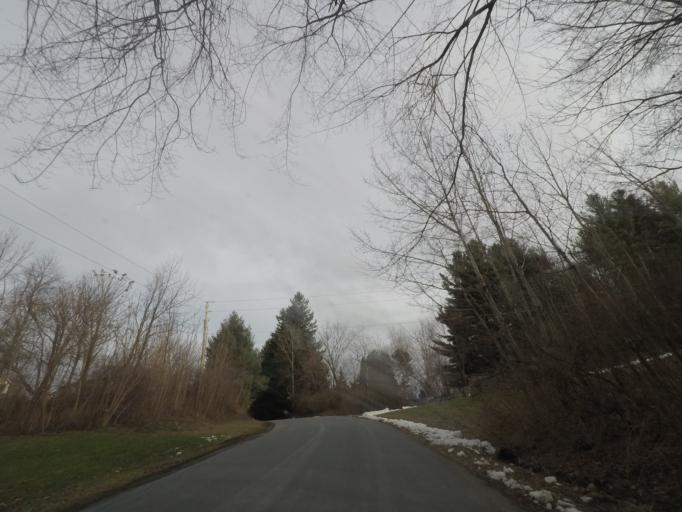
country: US
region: New York
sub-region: Rensselaer County
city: West Sand Lake
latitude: 42.6430
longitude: -73.6392
